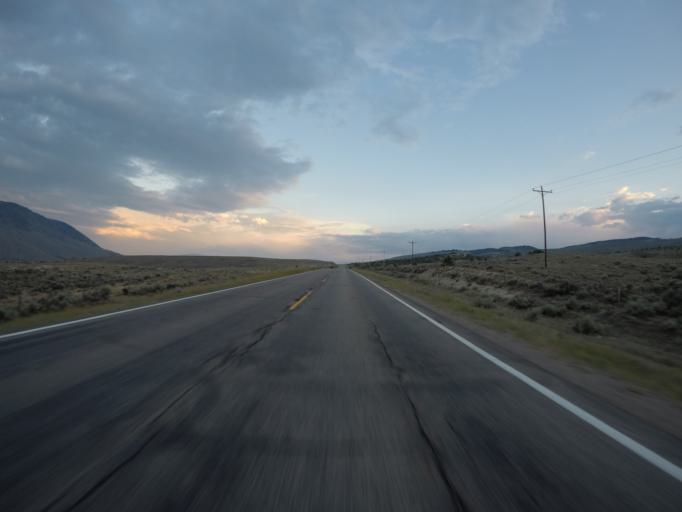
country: US
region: Colorado
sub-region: Grand County
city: Kremmling
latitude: 40.1242
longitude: -106.4298
